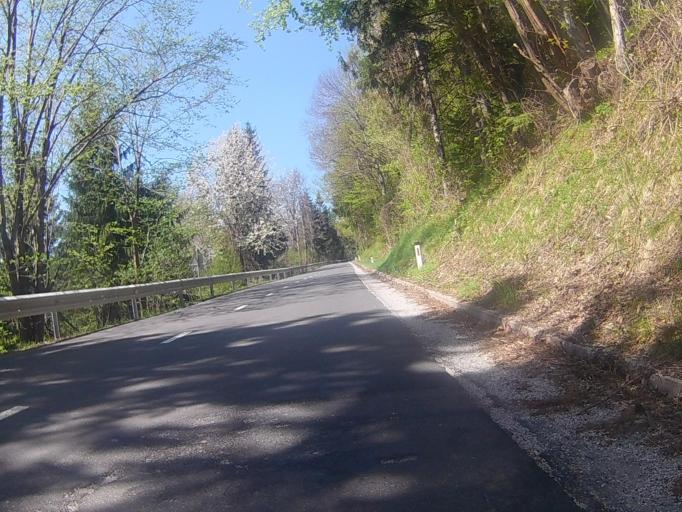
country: SI
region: Race-Fram
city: Morje
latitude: 46.4846
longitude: 15.5746
